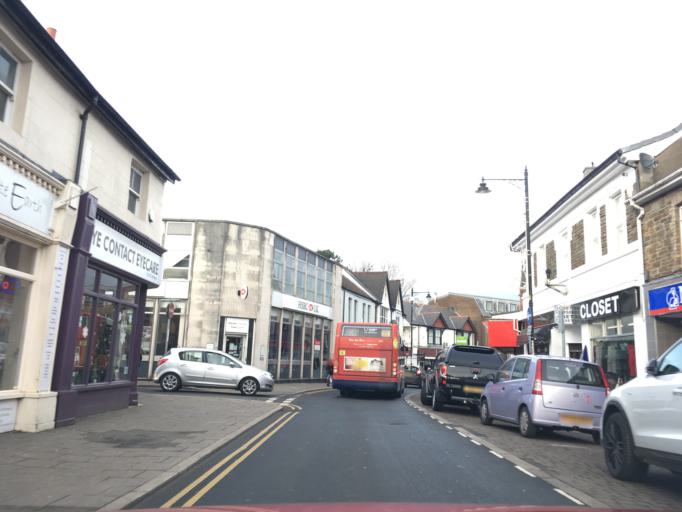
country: GB
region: Wales
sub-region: Caerphilly County Borough
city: Caerphilly
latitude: 51.5738
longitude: -3.2203
